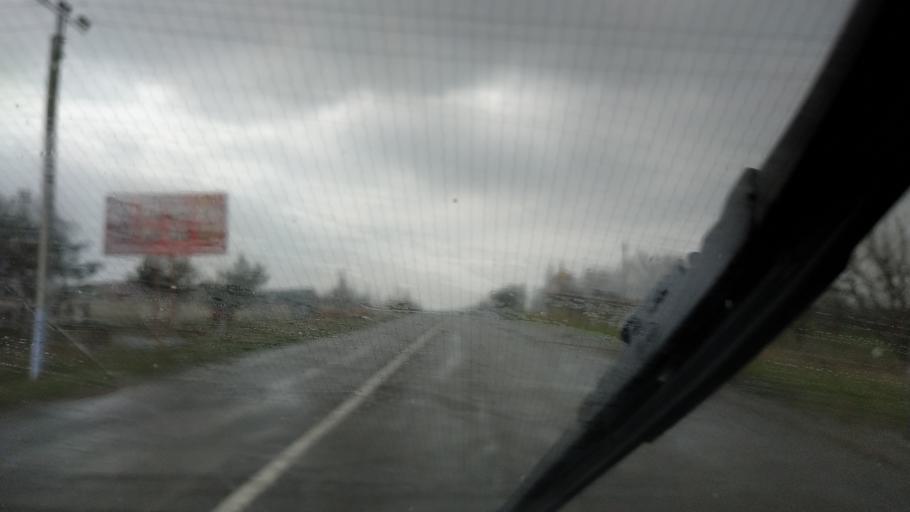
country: MD
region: Gagauzia
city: Comrat
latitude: 46.3054
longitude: 28.6248
